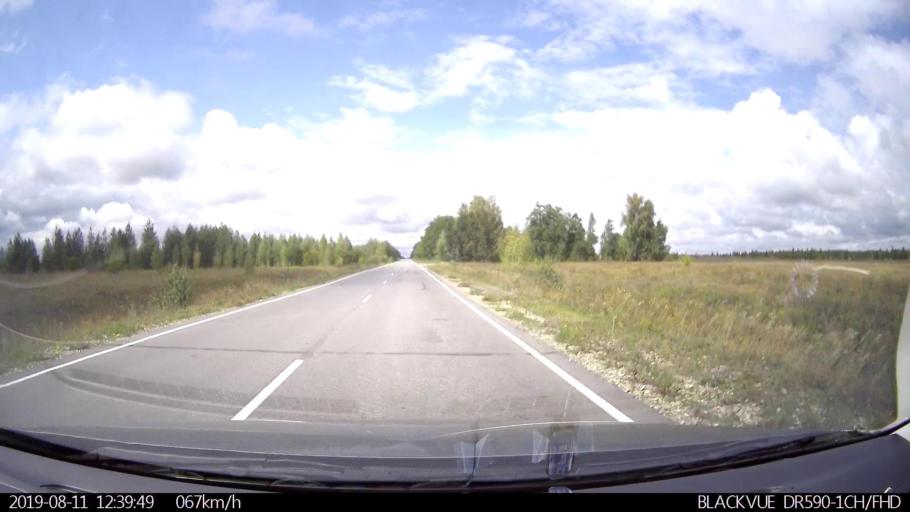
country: RU
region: Ulyanovsk
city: Ignatovka
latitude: 53.8353
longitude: 47.7899
